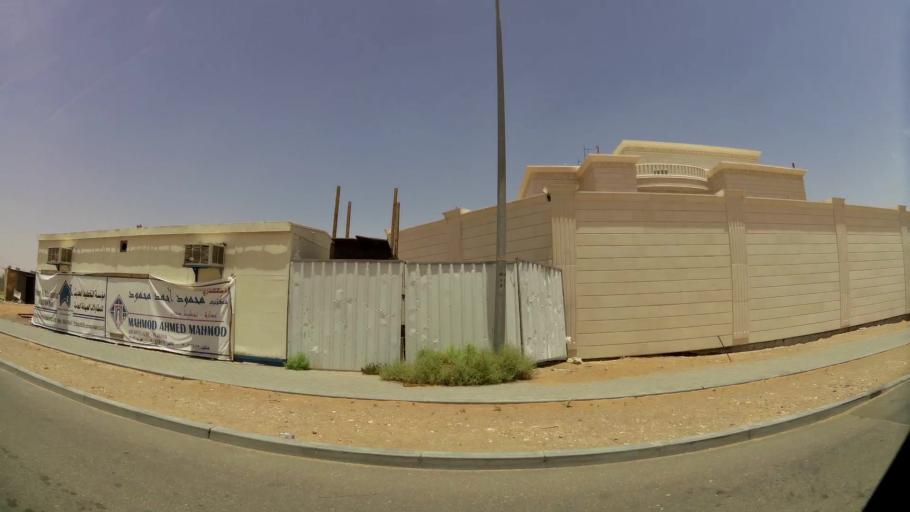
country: OM
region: Al Buraimi
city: Al Buraymi
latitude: 24.2696
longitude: 55.7098
